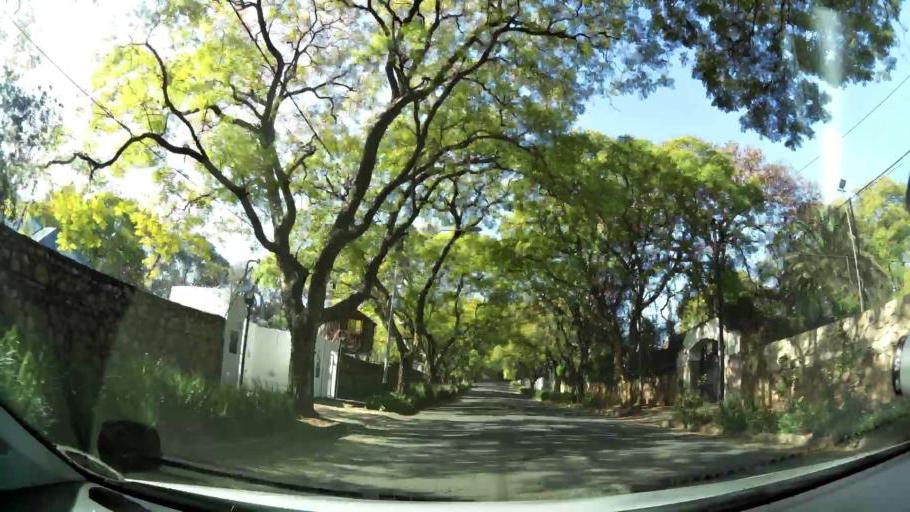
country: ZA
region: Gauteng
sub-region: City of Johannesburg Metropolitan Municipality
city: Johannesburg
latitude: -26.1711
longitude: 28.0770
